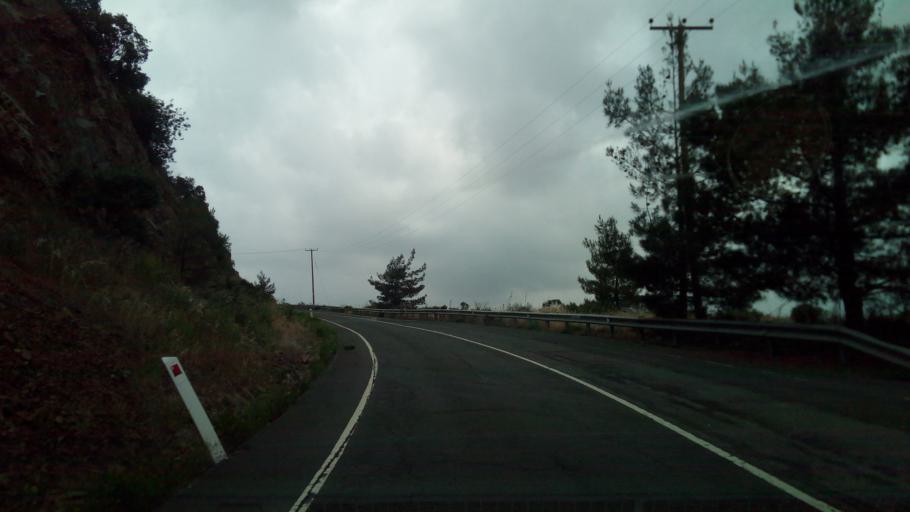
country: CY
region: Limassol
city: Pelendri
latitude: 34.8800
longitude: 32.9966
